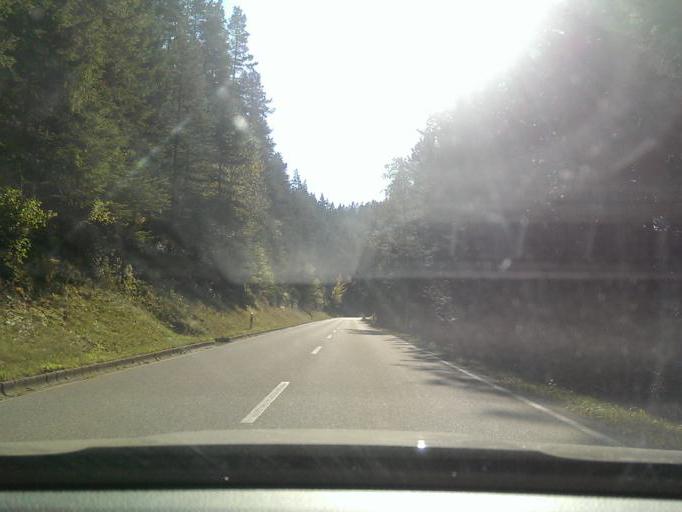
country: DE
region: Baden-Wuerttemberg
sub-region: Karlsruhe Region
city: Simmersfeld
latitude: 48.6575
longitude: 8.5354
